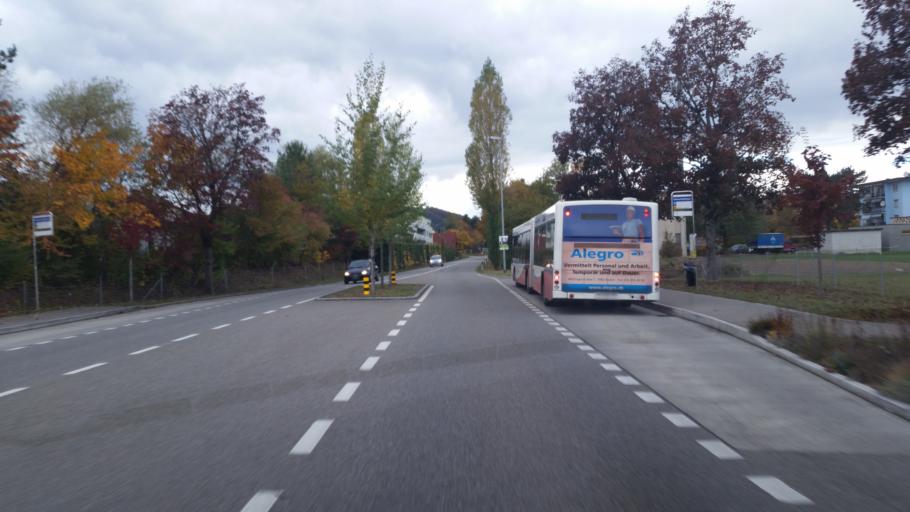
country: CH
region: Aargau
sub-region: Bezirk Baden
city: Untersiggenthal
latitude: 47.4988
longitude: 8.2572
